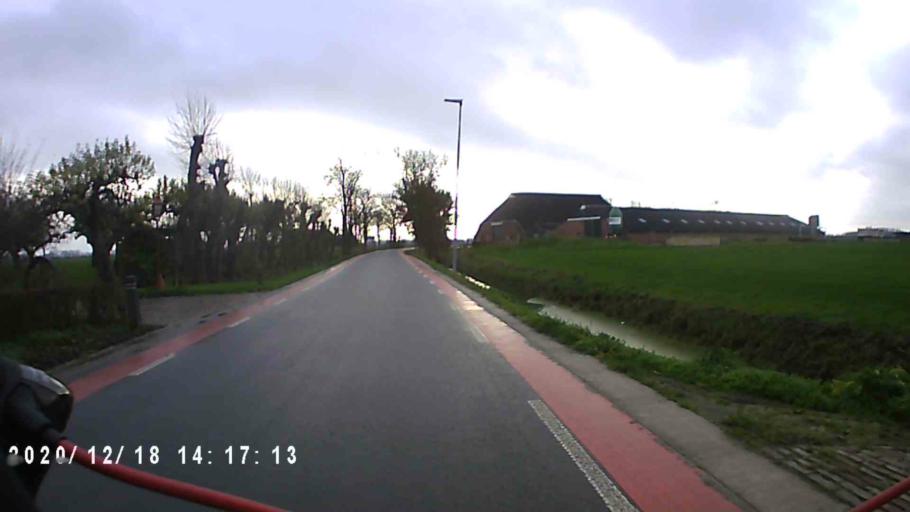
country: NL
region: Groningen
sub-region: Gemeente Bedum
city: Bedum
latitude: 53.2626
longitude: 6.6446
